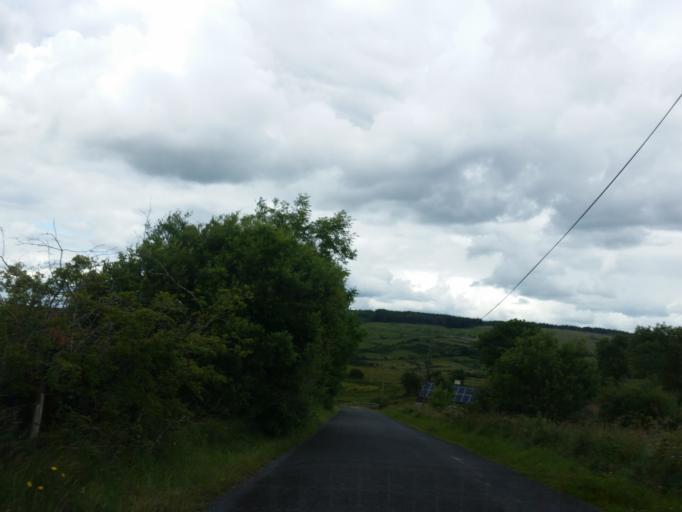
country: GB
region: Northern Ireland
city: Fivemiletown
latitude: 54.2858
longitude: -7.2763
